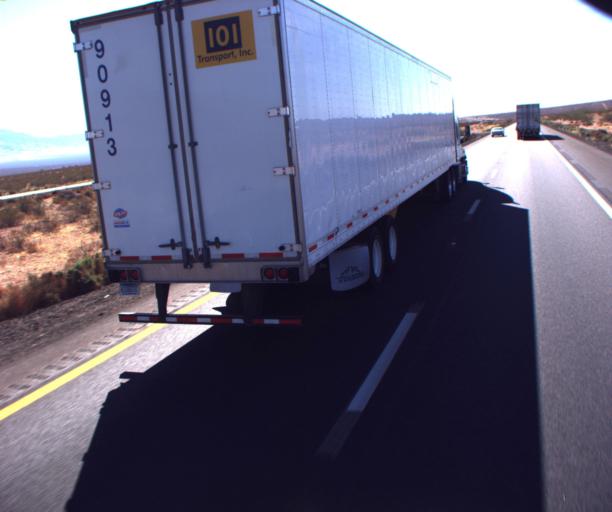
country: US
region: Arizona
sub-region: Mohave County
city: Beaver Dam
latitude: 36.8694
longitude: -113.9652
